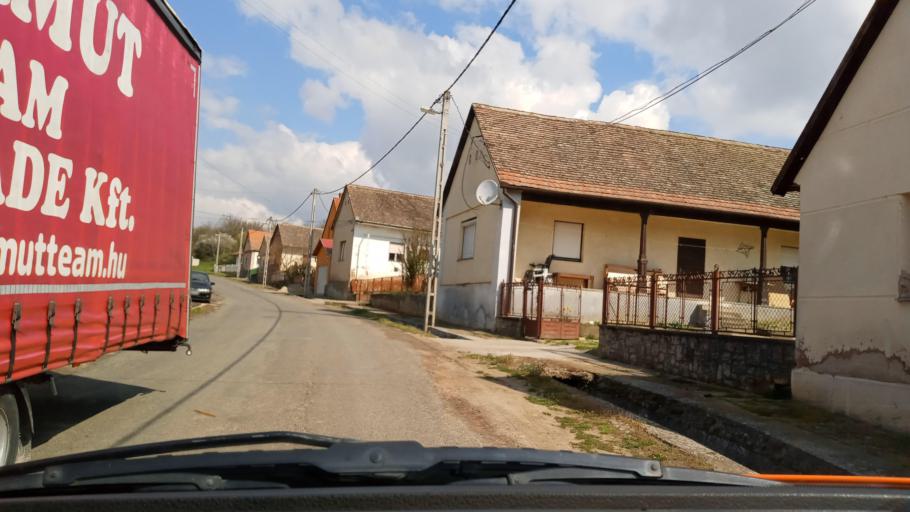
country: HU
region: Baranya
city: Boly
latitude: 46.0773
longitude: 18.5136
